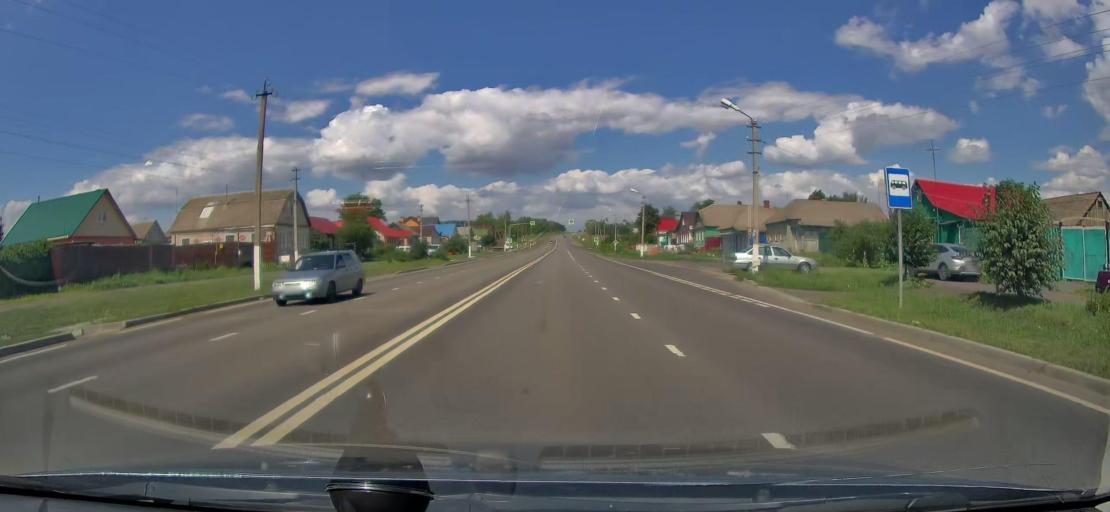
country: RU
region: Kursk
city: Zolotukhino
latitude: 51.9489
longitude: 36.3044
